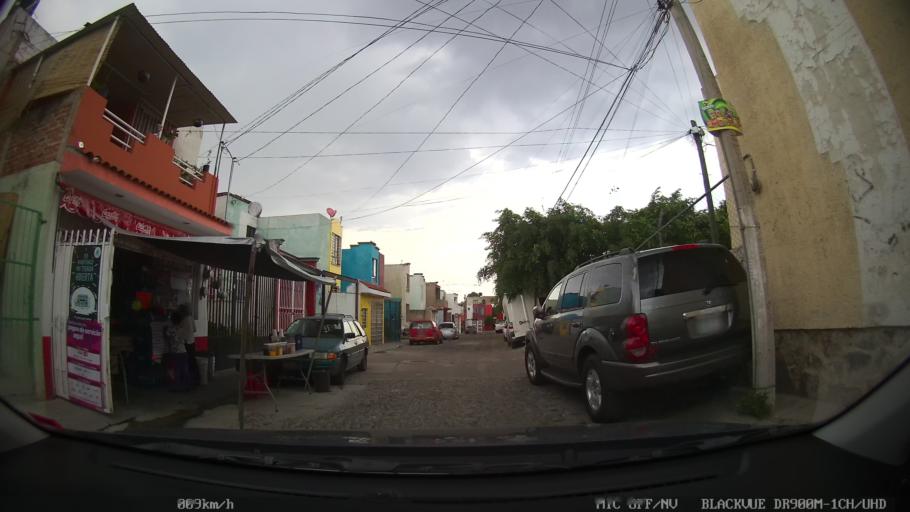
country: MX
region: Jalisco
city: Tlaquepaque
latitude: 20.6247
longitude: -103.2784
